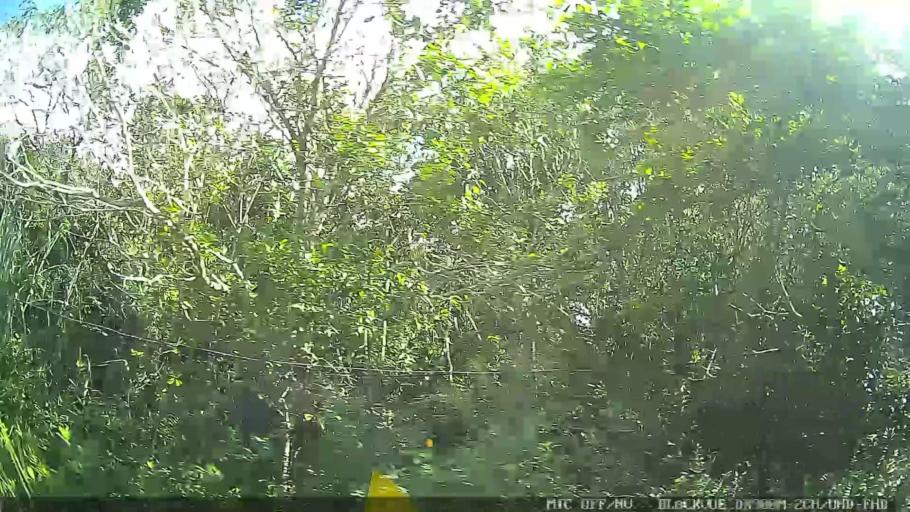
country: BR
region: Sao Paulo
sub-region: Peruibe
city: Peruibe
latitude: -24.2696
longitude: -46.9330
